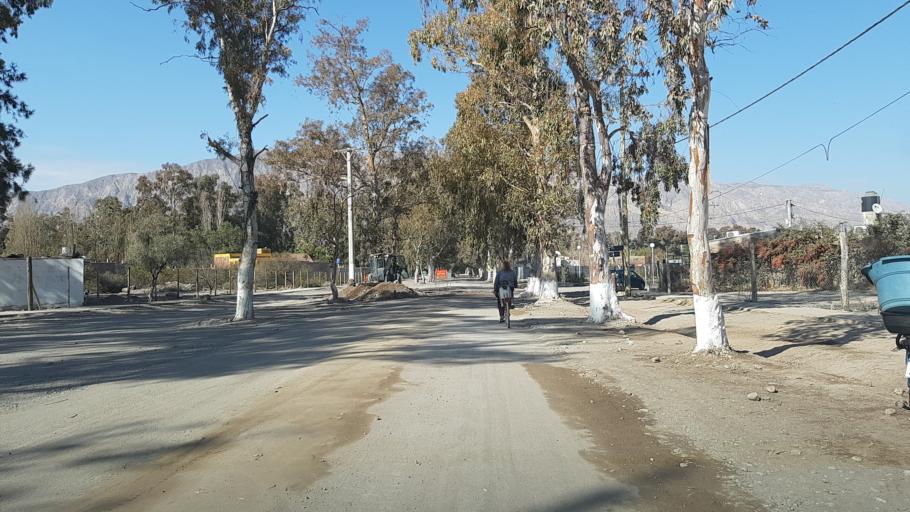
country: AR
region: San Juan
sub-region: Departamento de Zonda
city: Zonda
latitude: -31.5504
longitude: -68.7319
